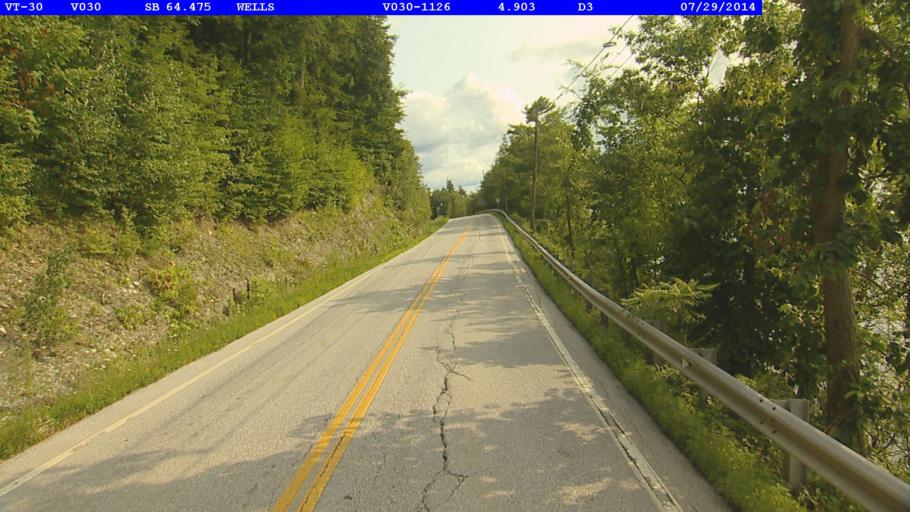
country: US
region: Vermont
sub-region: Rutland County
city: Poultney
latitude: 43.4614
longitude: -73.2056
